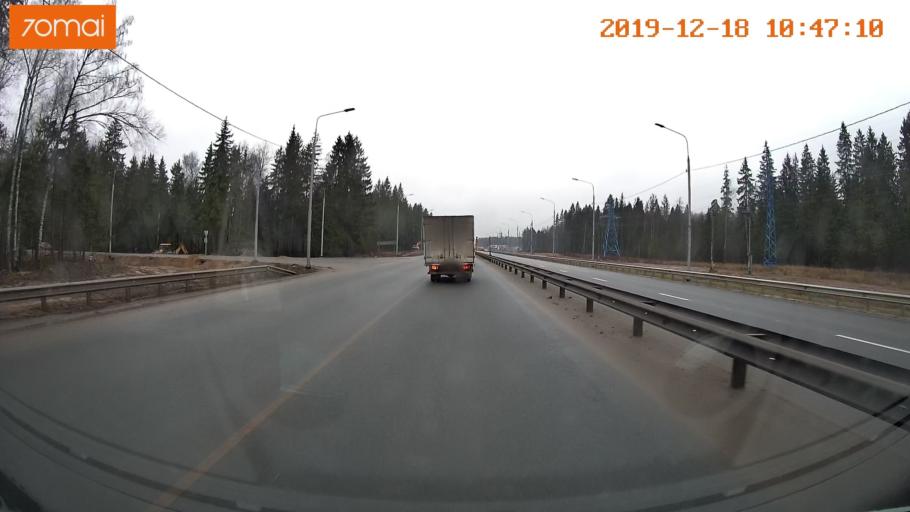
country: RU
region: Moskovskaya
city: Selyatino
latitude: 55.4890
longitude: 37.0403
